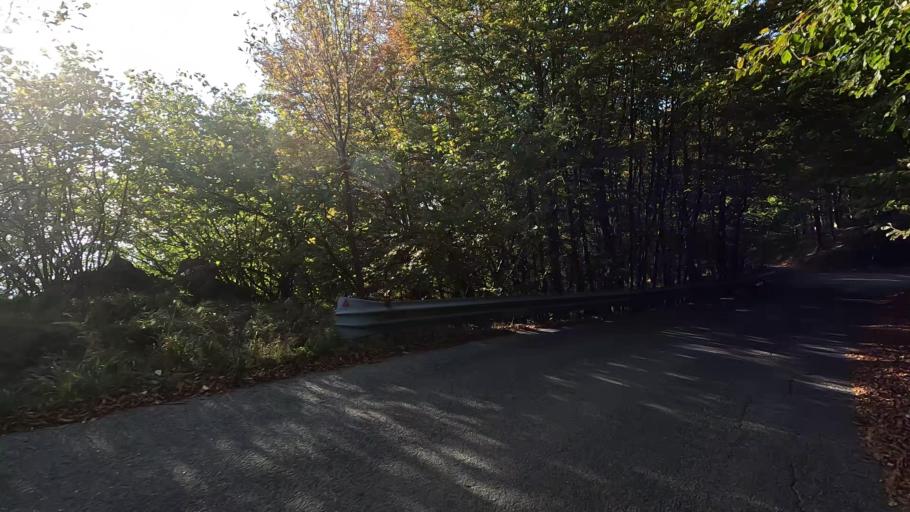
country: IT
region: Liguria
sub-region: Provincia di Savona
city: Urbe
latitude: 44.4293
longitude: 8.5548
